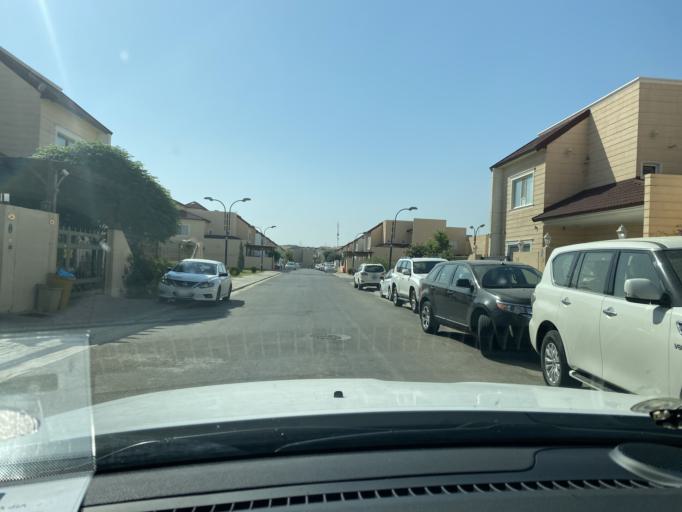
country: IQ
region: Arbil
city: Erbil
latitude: 36.2438
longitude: 44.0494
